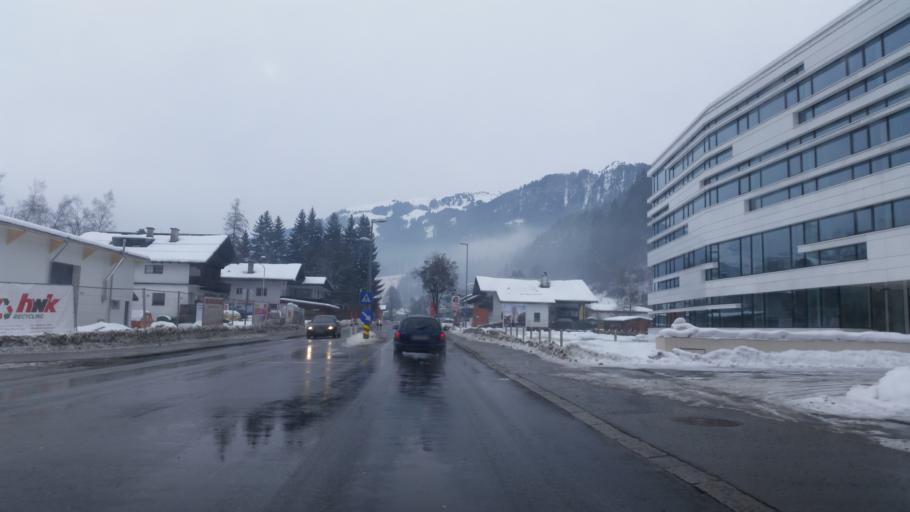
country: AT
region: Tyrol
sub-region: Politischer Bezirk Kitzbuhel
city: Kitzbuhel
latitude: 47.4622
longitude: 12.3862
